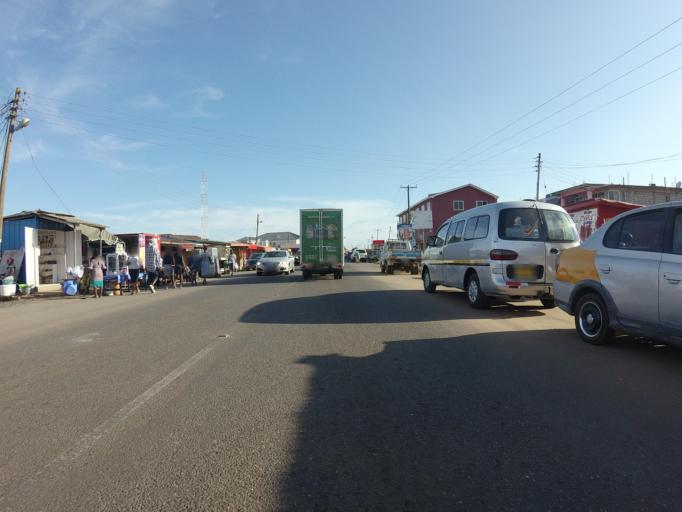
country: GH
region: Greater Accra
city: Nungua
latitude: 5.6310
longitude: -0.0900
